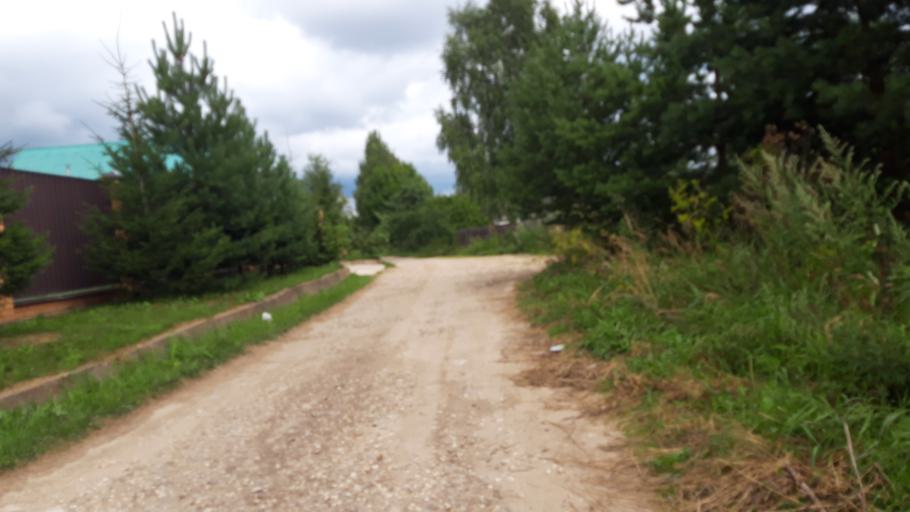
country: RU
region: Tverskaya
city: Konakovo
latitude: 56.6730
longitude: 36.7206
